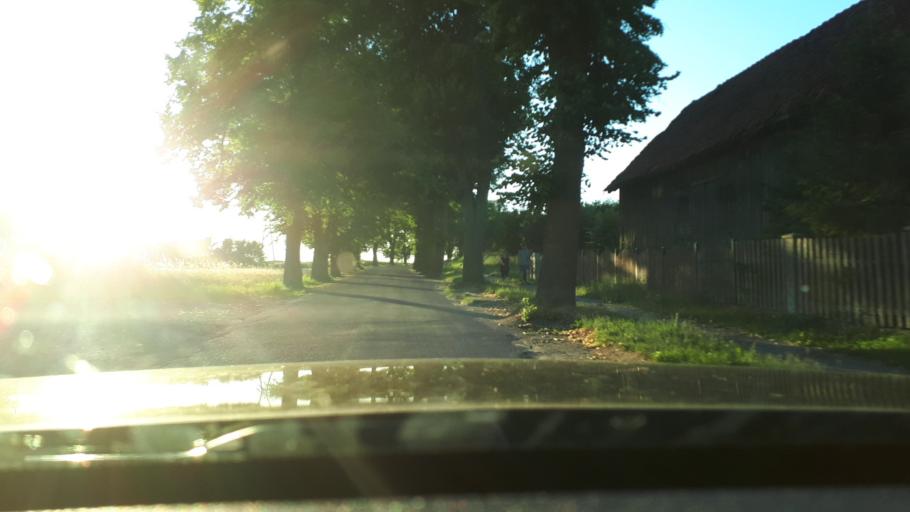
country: PL
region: Warmian-Masurian Voivodeship
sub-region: Powiat olsztynski
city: Olsztynek
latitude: 53.5902
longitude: 20.2766
